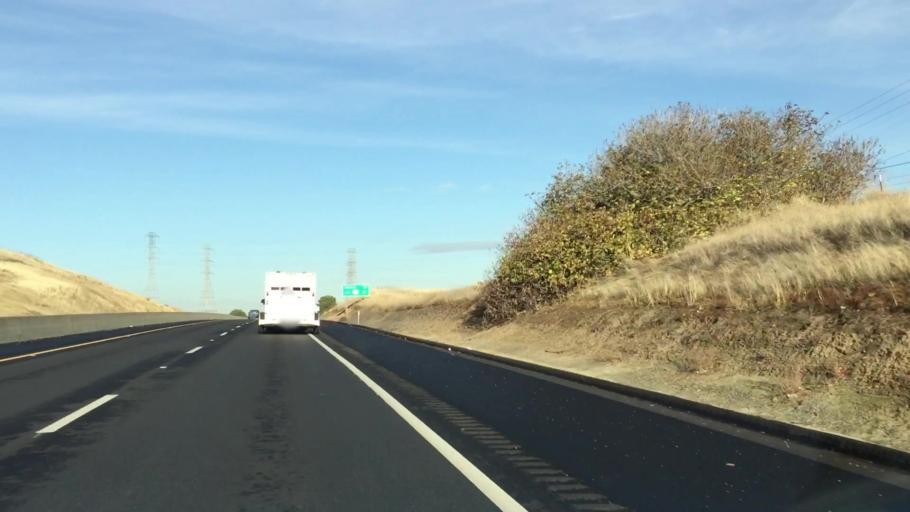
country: US
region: California
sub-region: Butte County
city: Thermalito
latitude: 39.5432
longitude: -121.5900
